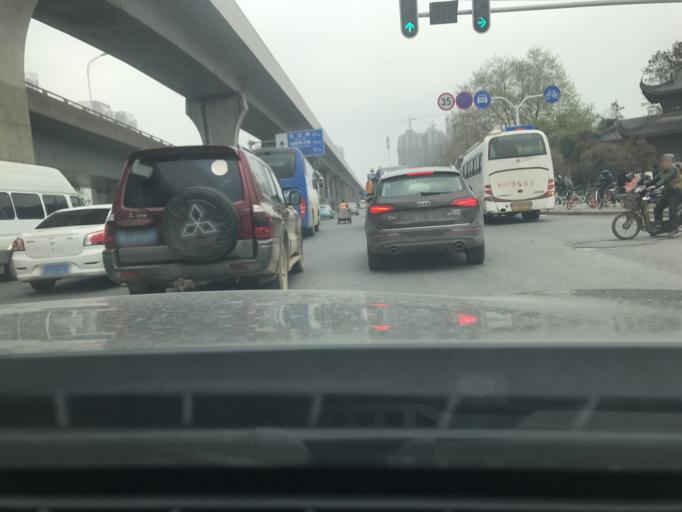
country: CN
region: Hubei
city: Houhu
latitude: 30.6607
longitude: 114.3301
